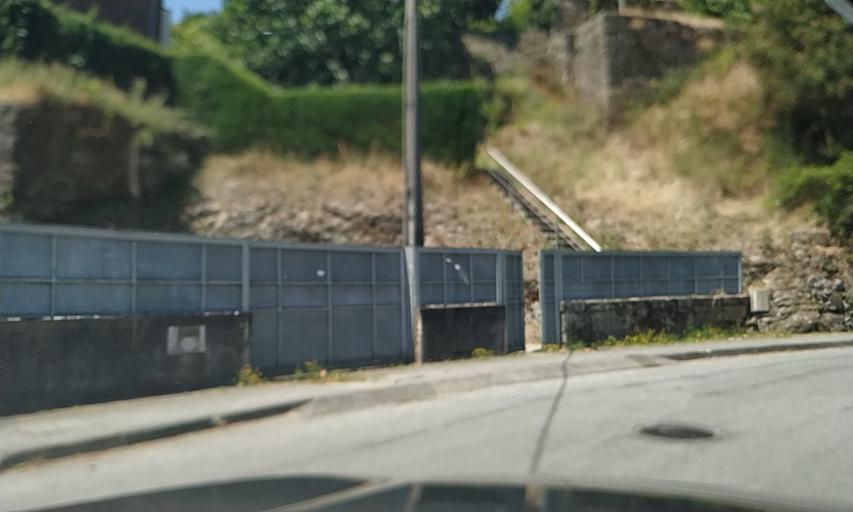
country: PT
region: Porto
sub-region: Amarante
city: Amarante
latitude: 41.2636
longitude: -8.0796
